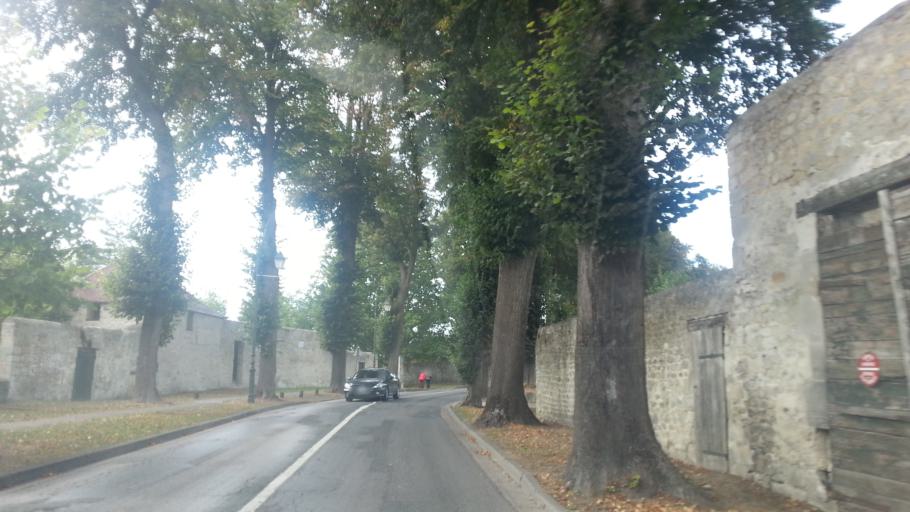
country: FR
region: Picardie
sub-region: Departement de l'Oise
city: Senlis
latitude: 49.2030
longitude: 2.5819
